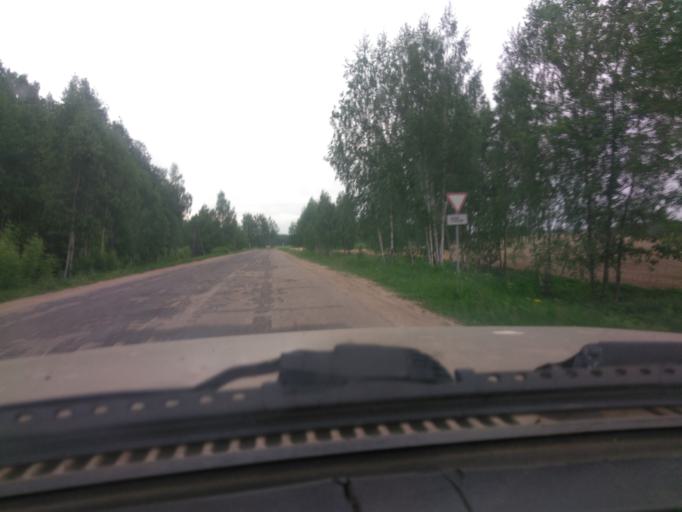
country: BY
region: Mogilev
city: Myazhysyatki
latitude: 53.8037
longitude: 30.0420
